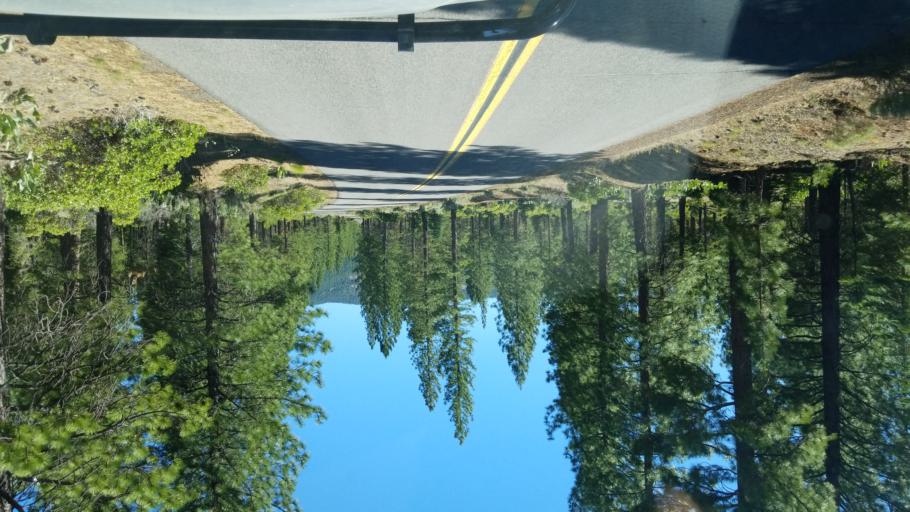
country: US
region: California
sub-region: Lassen County
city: Susanville
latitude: 40.5320
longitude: -120.7767
